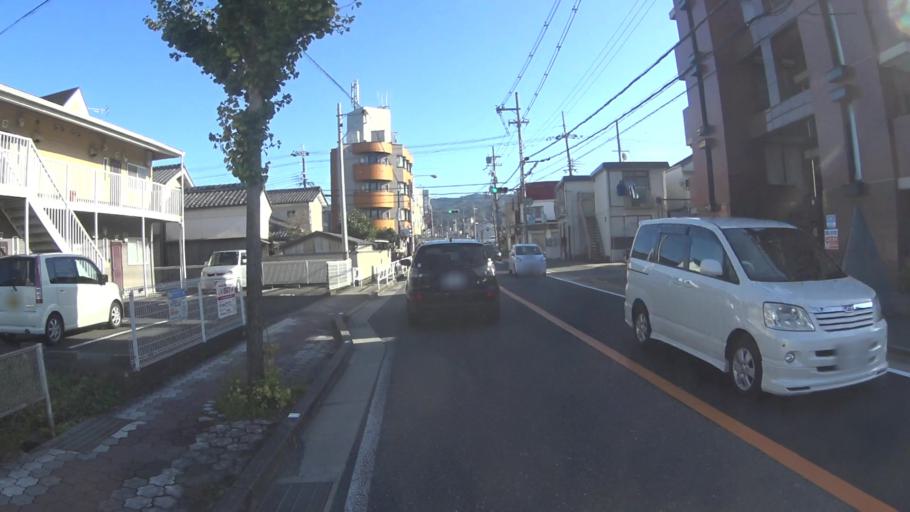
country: JP
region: Kyoto
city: Kameoka
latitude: 35.0097
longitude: 135.5883
